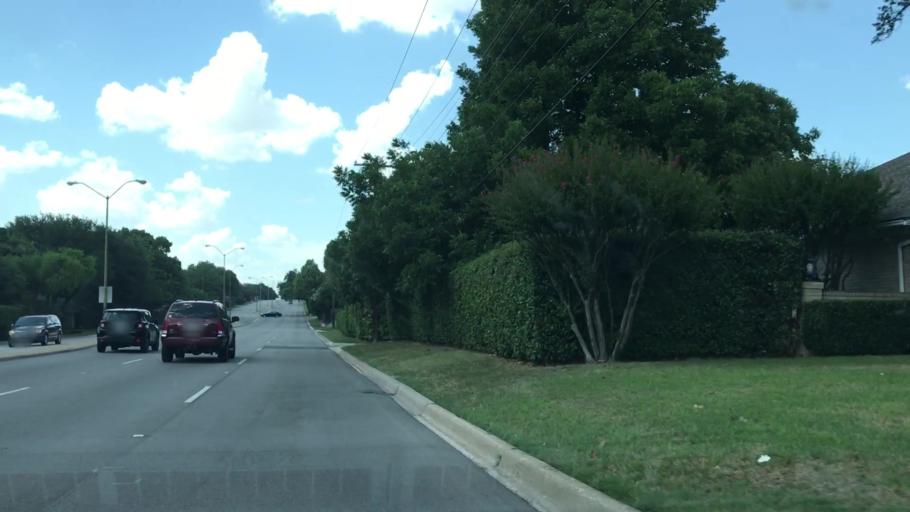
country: US
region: Texas
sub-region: Dallas County
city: Addison
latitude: 32.9121
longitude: -96.8381
